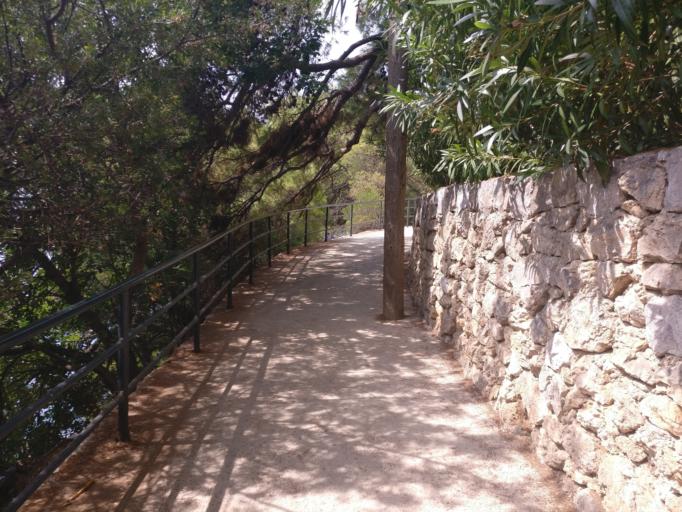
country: HR
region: Dubrovacko-Neretvanska
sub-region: Grad Dubrovnik
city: Dubrovnik
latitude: 42.6565
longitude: 18.0674
